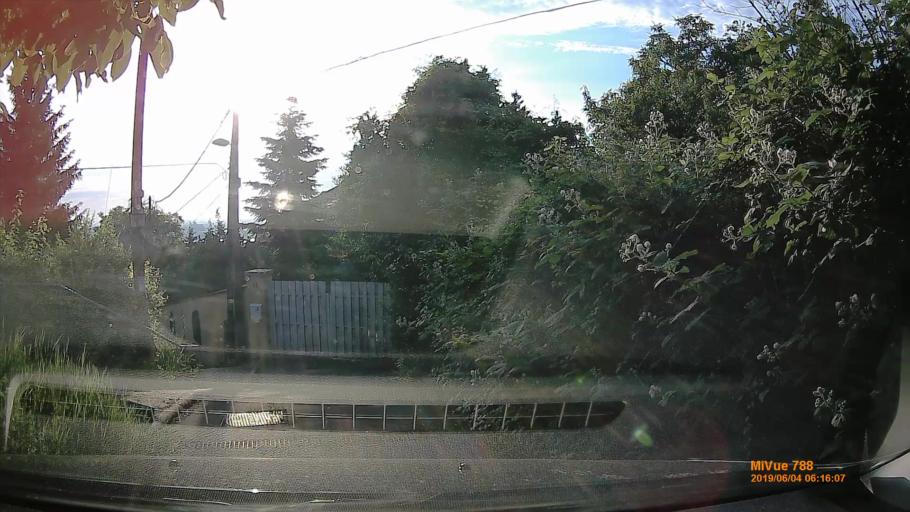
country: HU
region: Budapest
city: Budapest XXII. keruelet
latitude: 47.4339
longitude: 19.0298
